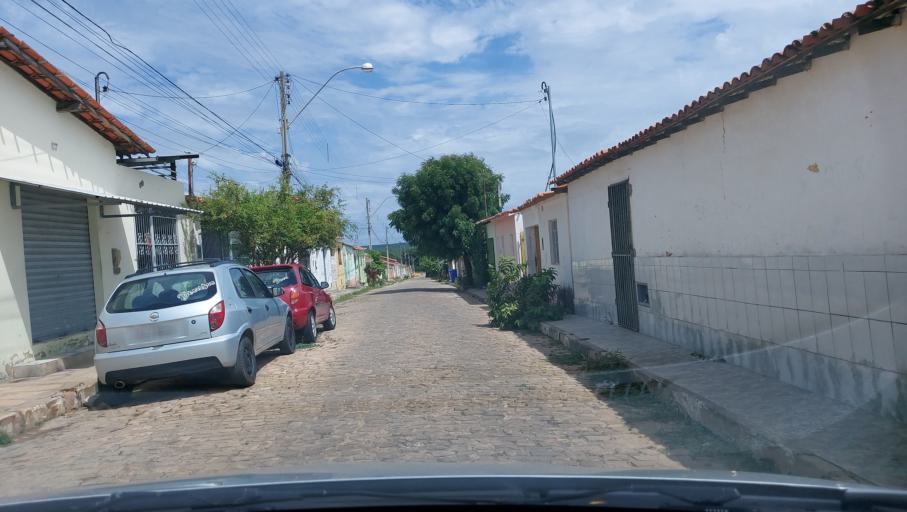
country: BR
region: Bahia
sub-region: Oliveira Dos Brejinhos
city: Beira Rio
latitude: -11.9982
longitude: -42.6281
